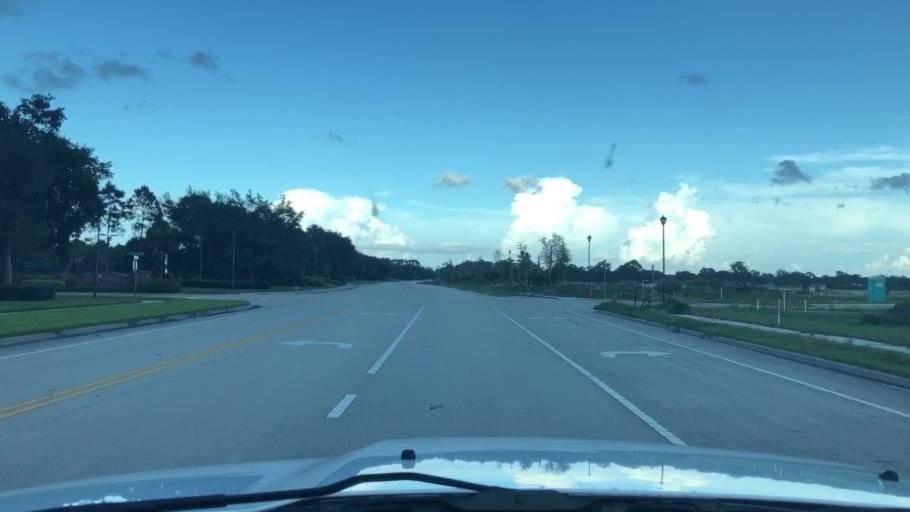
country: US
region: Florida
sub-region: Saint Lucie County
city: Lakewood Park
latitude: 27.5652
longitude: -80.4128
